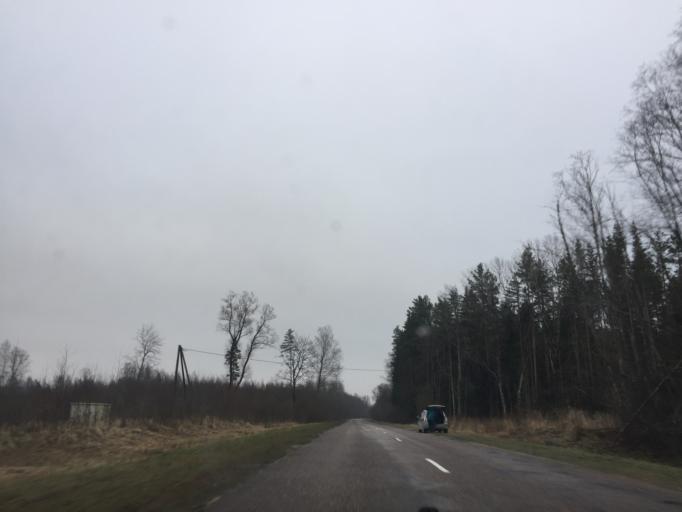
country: LV
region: Limbazu Rajons
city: Limbazi
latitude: 57.5446
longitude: 24.6779
